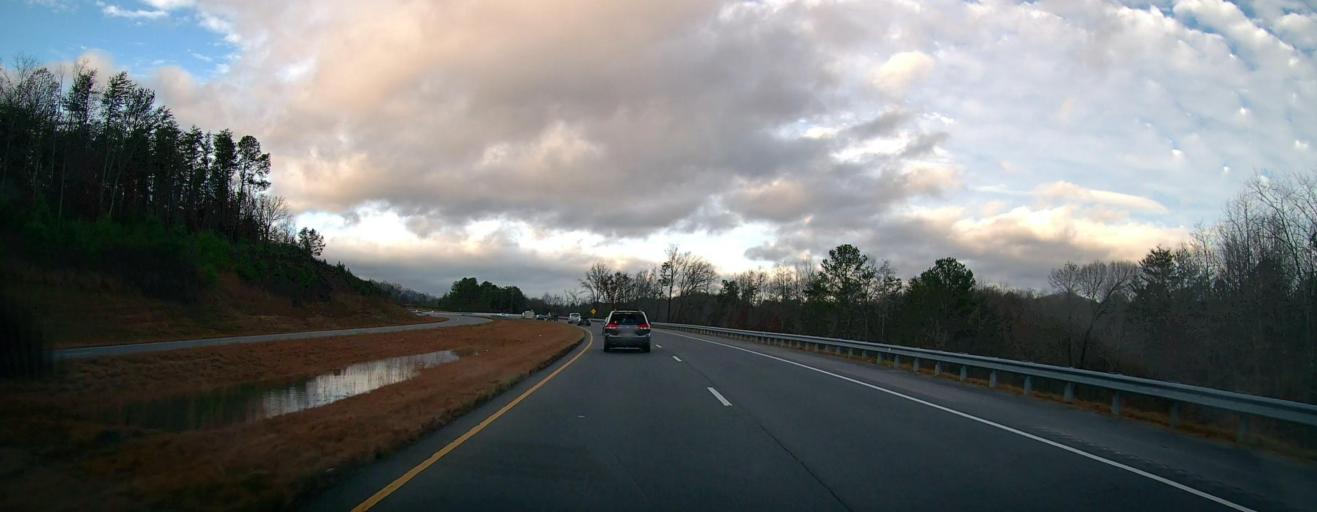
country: US
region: Georgia
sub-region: White County
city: Cleveland
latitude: 34.5968
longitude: -83.7813
